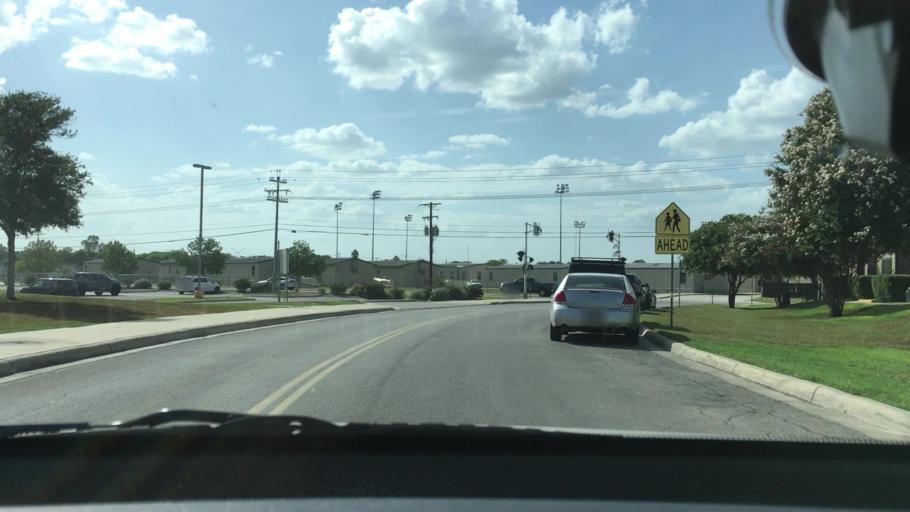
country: US
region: Texas
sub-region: Guadalupe County
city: Schertz
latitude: 29.5614
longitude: -98.2652
